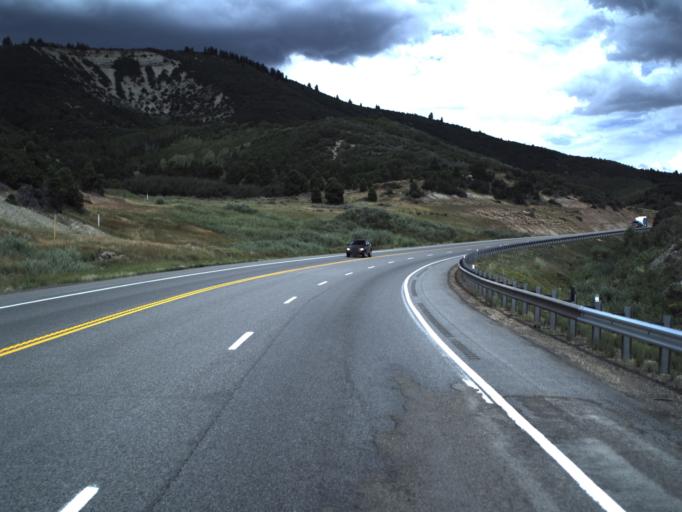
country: US
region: Utah
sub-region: Carbon County
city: Helper
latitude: 39.9338
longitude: -111.1055
